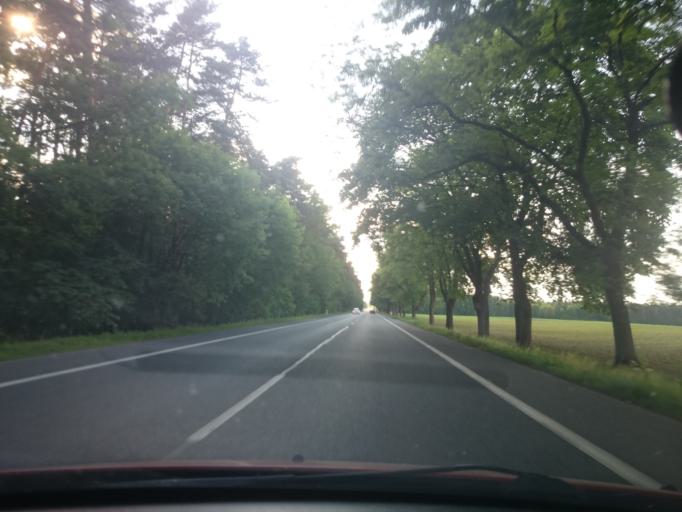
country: PL
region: Opole Voivodeship
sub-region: Powiat strzelecki
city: Strzelce Opolskie
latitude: 50.5451
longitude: 18.2363
